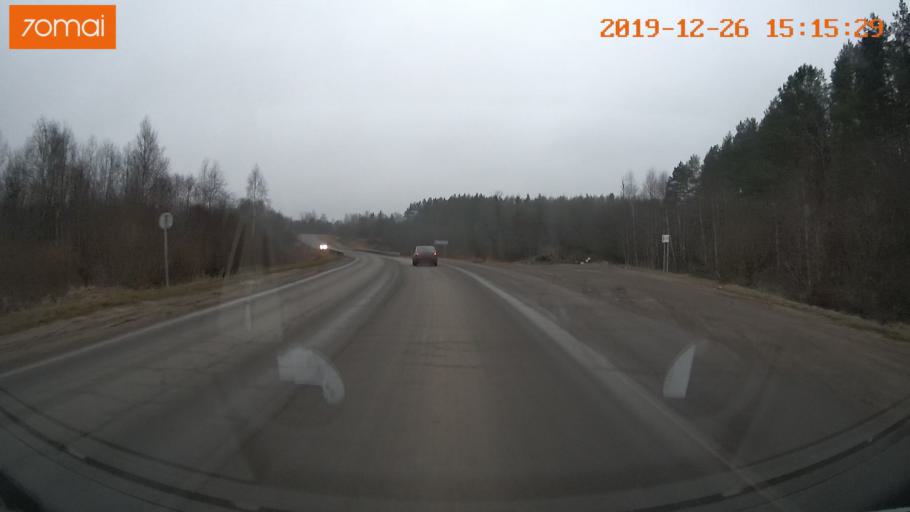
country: RU
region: Jaroslavl
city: Rybinsk
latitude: 58.0964
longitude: 38.8744
